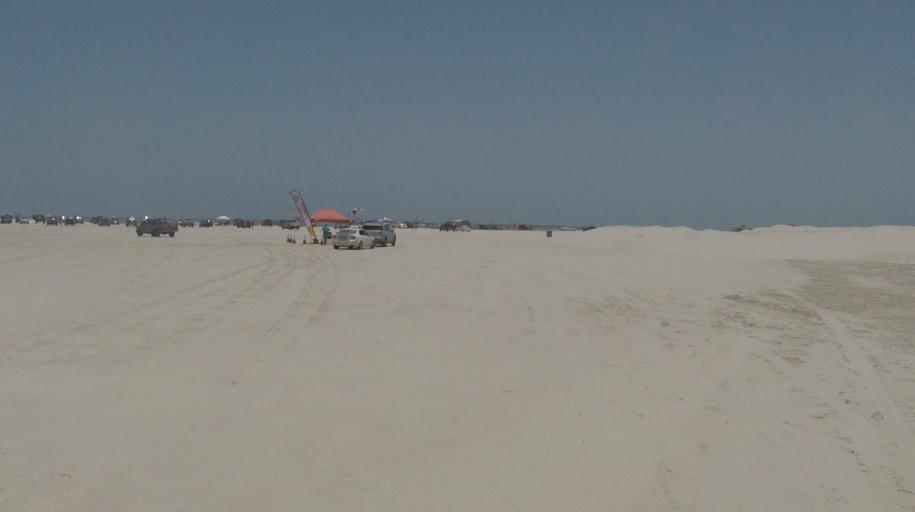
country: US
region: Texas
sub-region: Nueces County
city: Port Aransas
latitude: 27.6169
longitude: -97.2022
